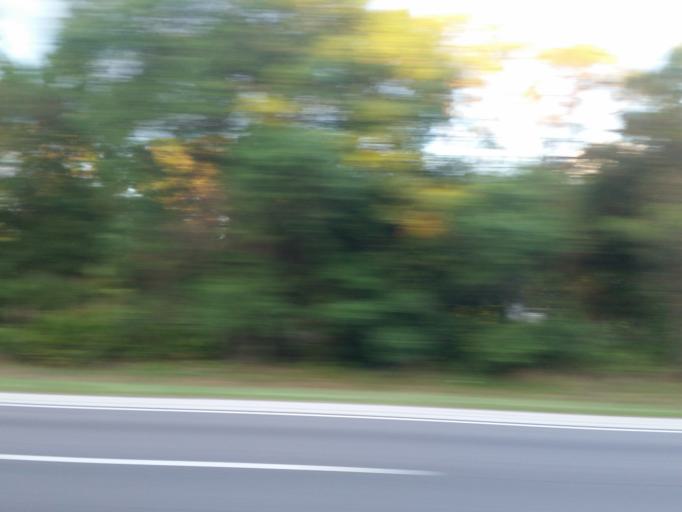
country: US
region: Florida
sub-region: Sarasota County
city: The Meadows
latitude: 27.3547
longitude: -82.4463
